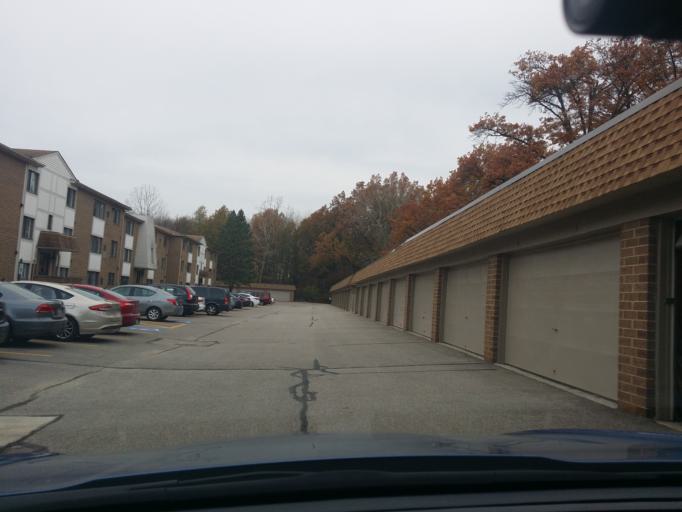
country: US
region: Ohio
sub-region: Cuyahoga County
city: North Olmsted
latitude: 41.4283
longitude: -81.8994
